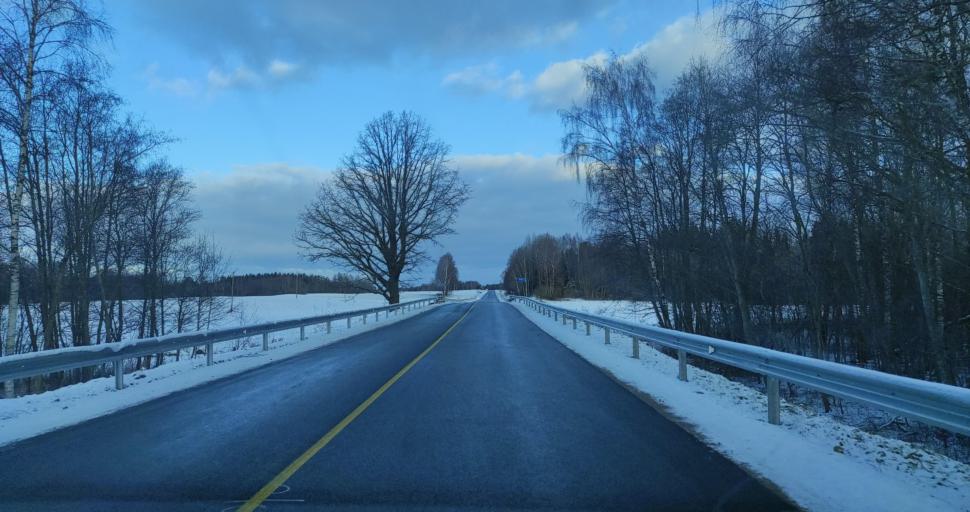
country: LV
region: Skrunda
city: Skrunda
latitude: 56.7134
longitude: 22.0117
